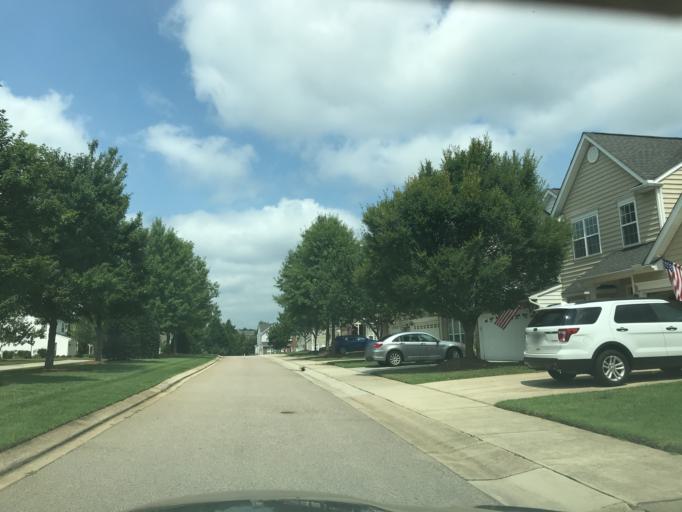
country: US
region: North Carolina
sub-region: Wake County
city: Wake Forest
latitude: 35.9303
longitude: -78.5607
